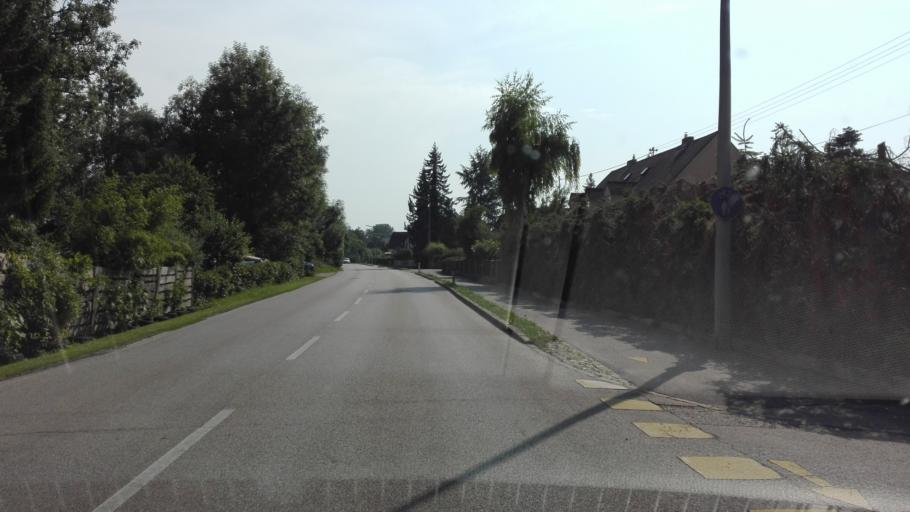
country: AT
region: Upper Austria
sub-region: Politischer Bezirk Linz-Land
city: Traun
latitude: 48.2272
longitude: 14.2603
